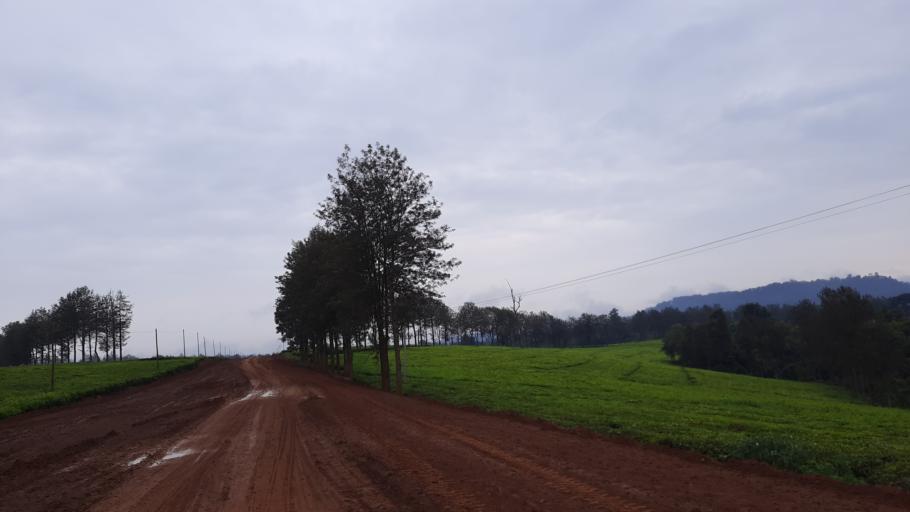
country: ET
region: Oromiya
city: Gore
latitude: 7.8492
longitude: 35.4763
